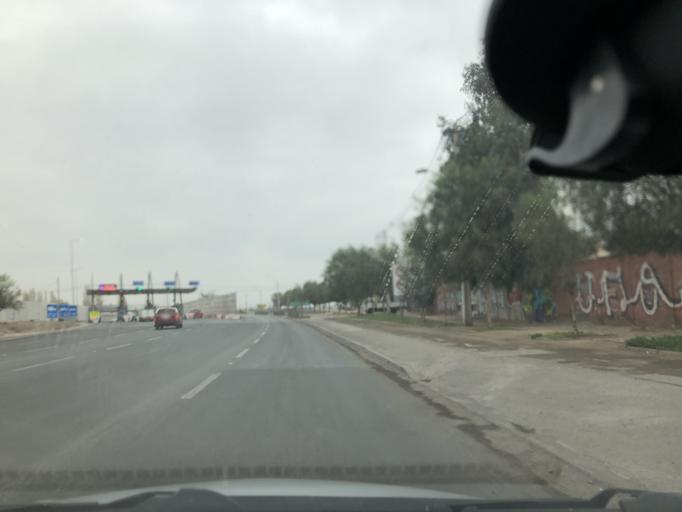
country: CL
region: Santiago Metropolitan
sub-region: Provincia de Santiago
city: La Pintana
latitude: -33.5826
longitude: -70.6098
